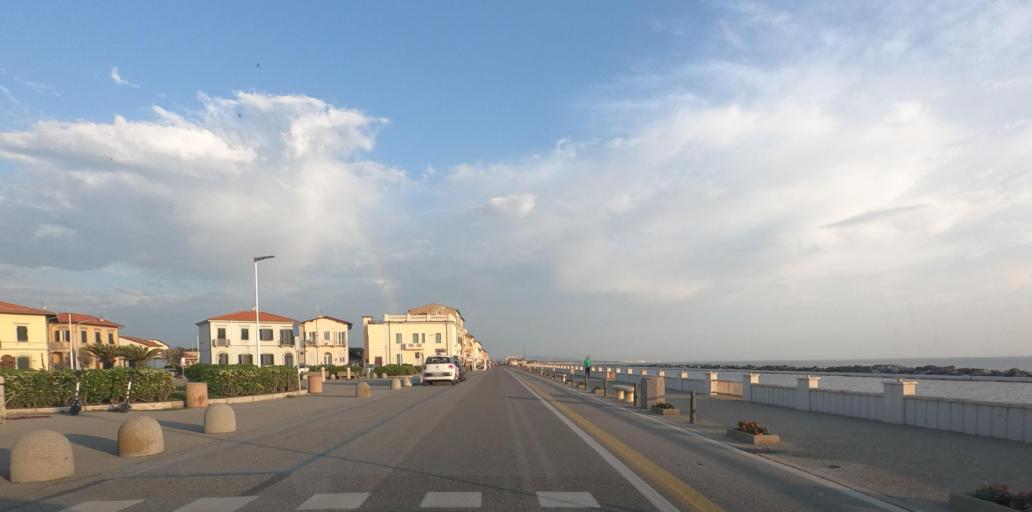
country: IT
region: Tuscany
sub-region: Province of Pisa
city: Marina di Pisa
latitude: 43.6634
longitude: 10.2776
